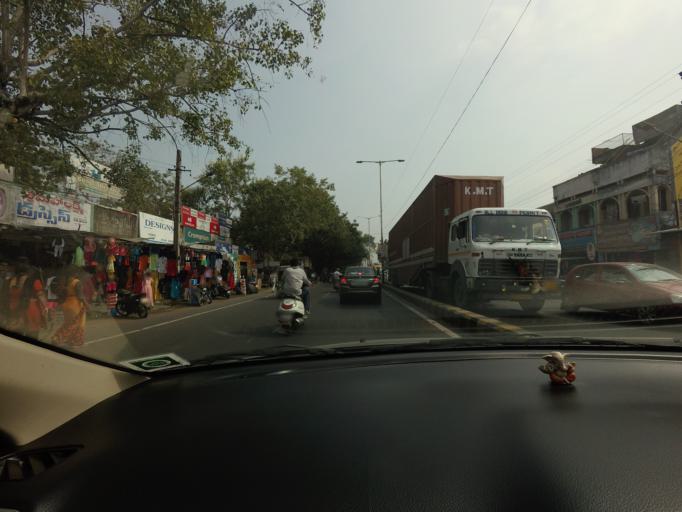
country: IN
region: Andhra Pradesh
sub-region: Krishna
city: Yanamalakuduru
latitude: 16.4945
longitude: 80.6624
